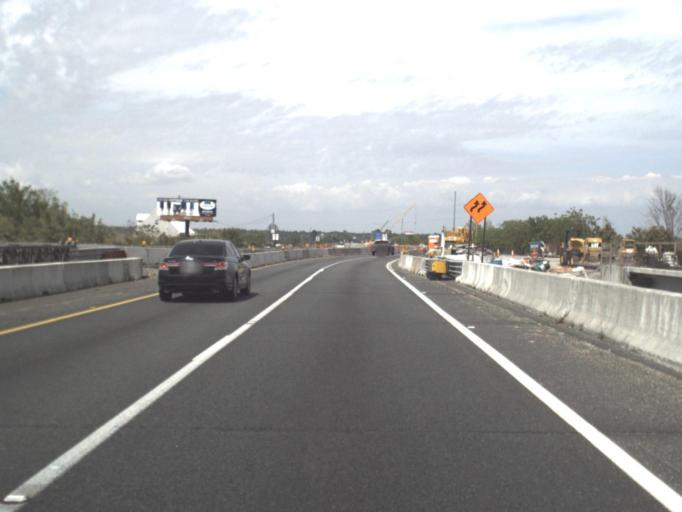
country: US
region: Florida
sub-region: Santa Rosa County
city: Pace
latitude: 30.5728
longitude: -87.1842
